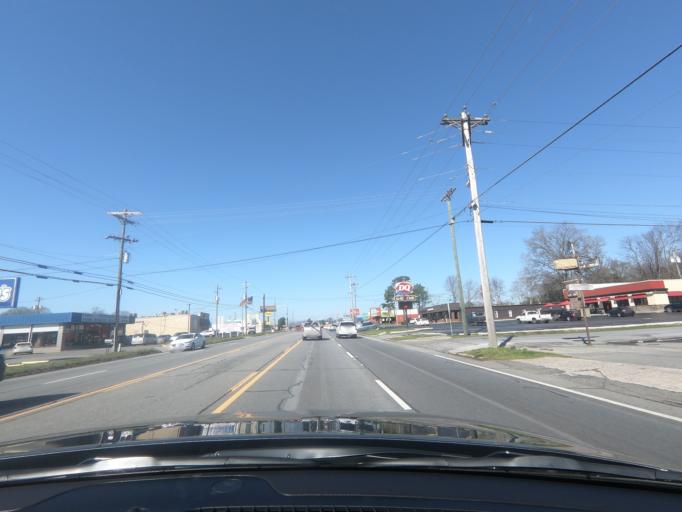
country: US
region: Georgia
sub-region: Gordon County
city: Calhoun
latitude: 34.4772
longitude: -84.9315
